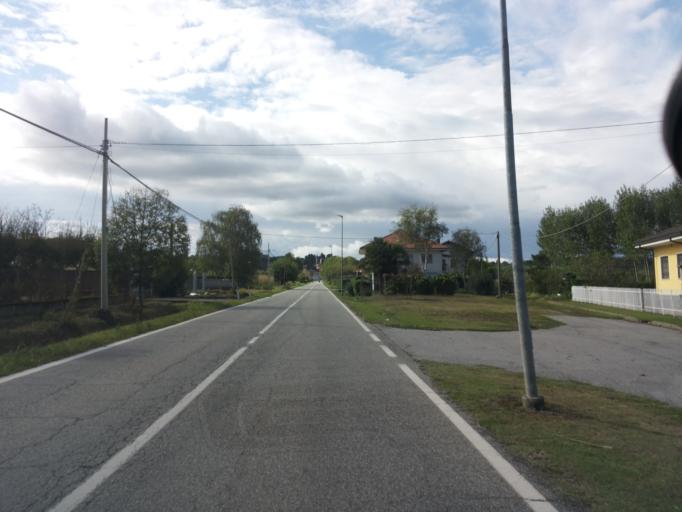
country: IT
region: Piedmont
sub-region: Provincia di Vercelli
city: Moncrivello
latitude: 45.3241
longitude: 8.0104
